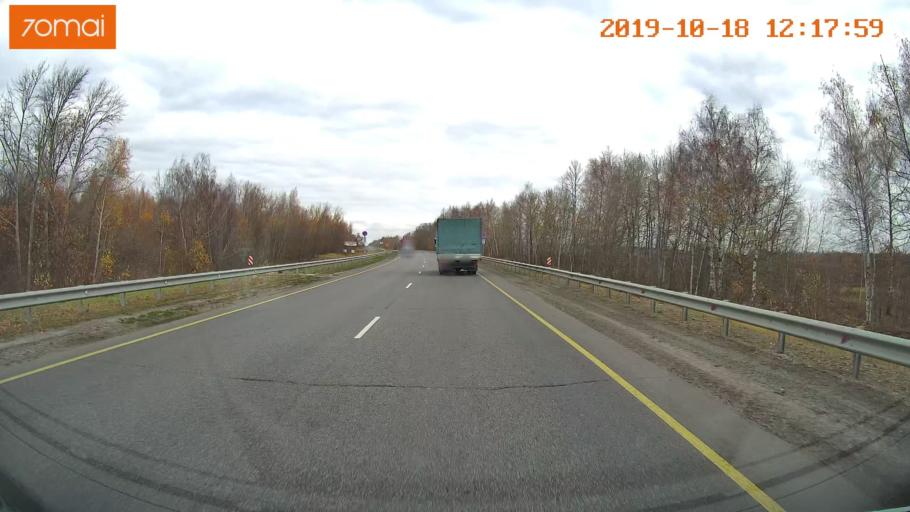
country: RU
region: Rjazan
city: Zakharovo
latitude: 54.4621
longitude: 39.4516
